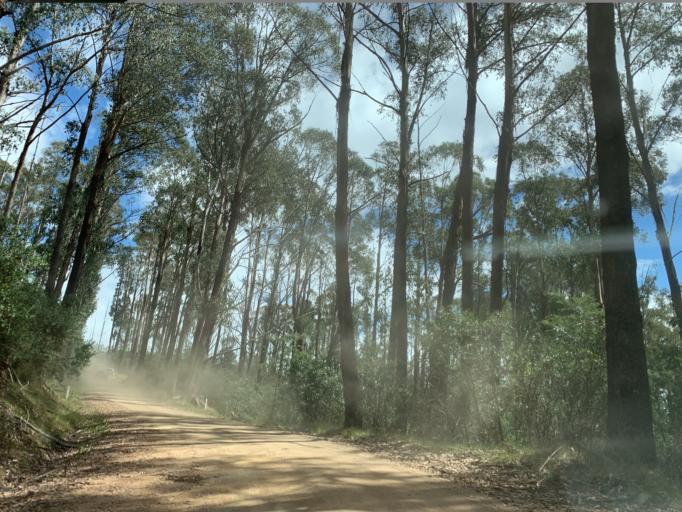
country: AU
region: Victoria
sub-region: Mansfield
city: Mansfield
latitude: -37.0967
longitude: 146.5355
